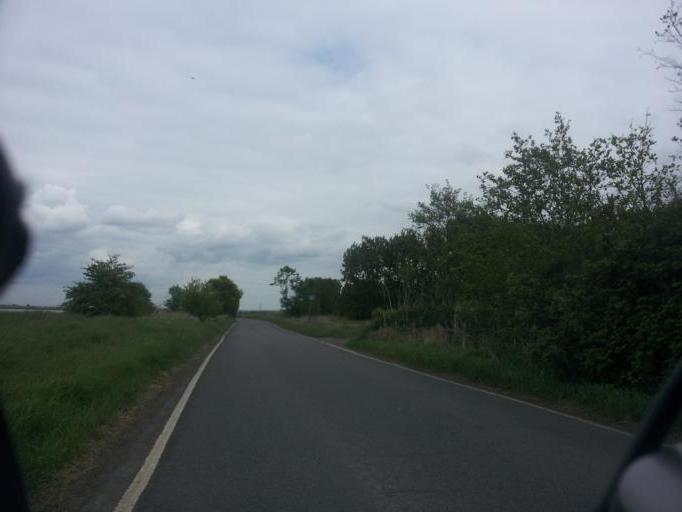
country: GB
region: England
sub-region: Kent
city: Newington
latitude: 51.3811
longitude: 0.7015
